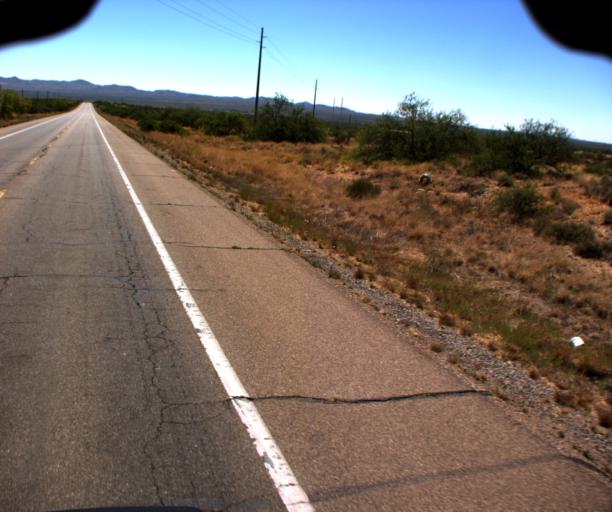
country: US
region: Arizona
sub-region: Pinal County
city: Oracle
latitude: 32.5994
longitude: -110.8745
